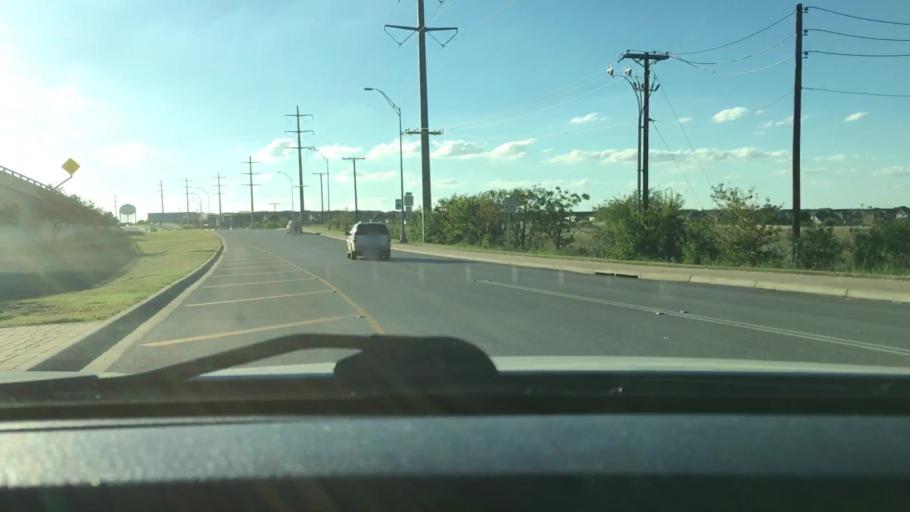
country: US
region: Texas
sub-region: Travis County
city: Windemere
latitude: 30.4888
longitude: -97.6297
